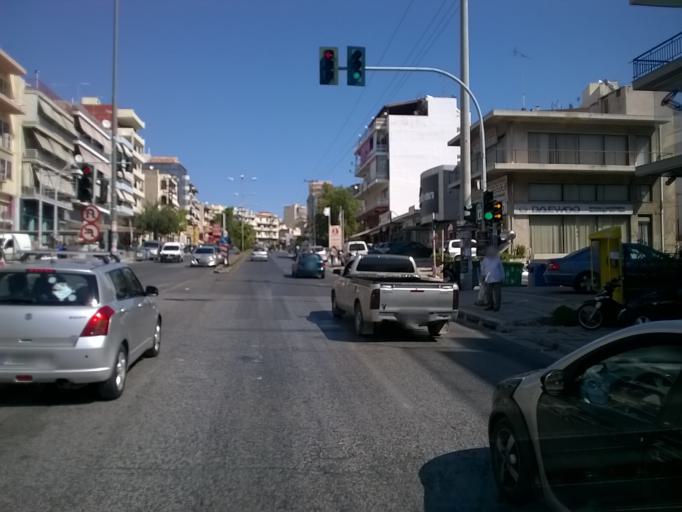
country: GR
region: Attica
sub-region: Nomos Piraios
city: Keratsini
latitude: 37.9761
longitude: 23.6269
